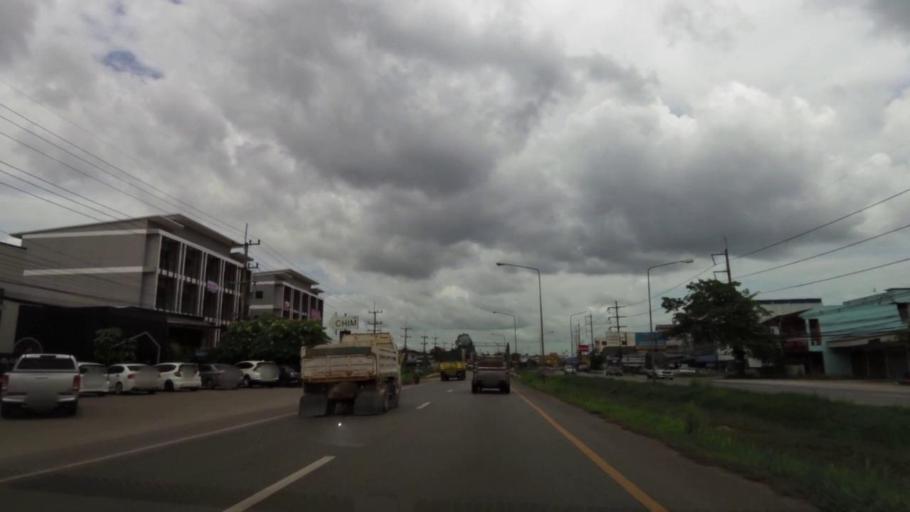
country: TH
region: Rayong
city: Klaeng
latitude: 12.7849
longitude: 101.6585
